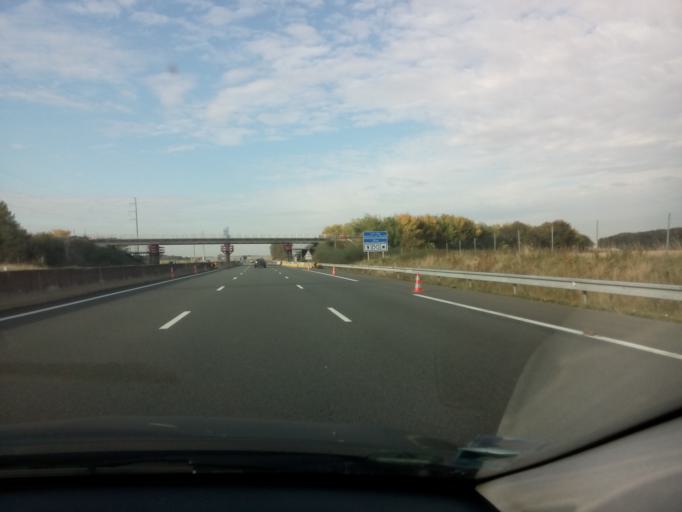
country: FR
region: Centre
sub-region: Departement d'Eure-et-Loir
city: Bailleau-le-Pin
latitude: 48.3150
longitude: 1.3234
